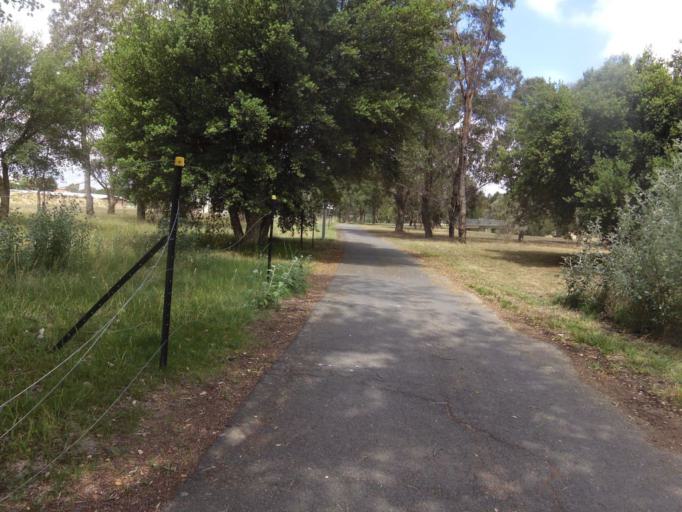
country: AU
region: Australian Capital Territory
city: Macarthur
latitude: -35.4212
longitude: 149.0836
